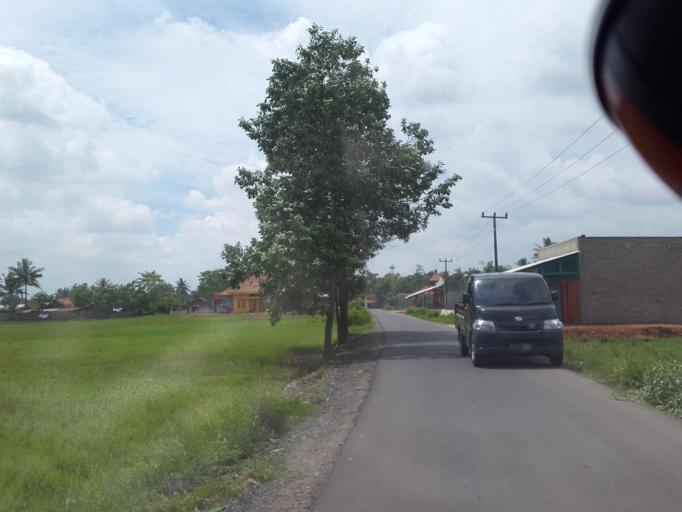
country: ID
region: Lampung
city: Natar
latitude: -5.3041
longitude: 105.2237
